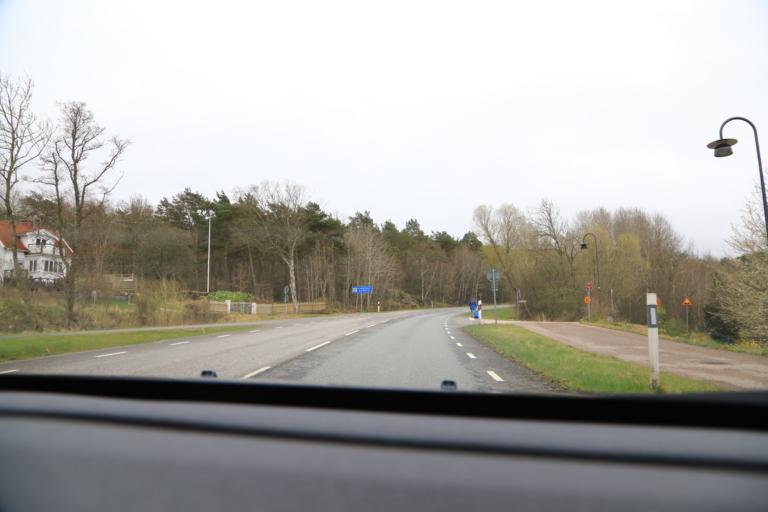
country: SE
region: Halland
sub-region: Kungsbacka Kommun
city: Frillesas
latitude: 57.3113
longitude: 12.1821
